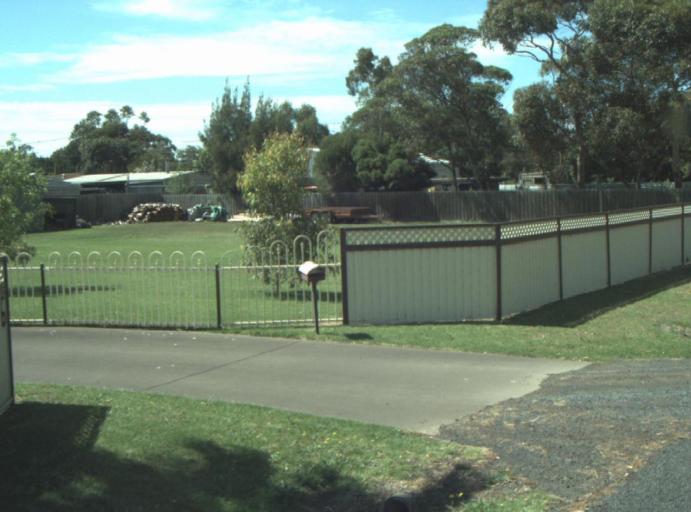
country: AU
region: Victoria
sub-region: Greater Geelong
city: East Geelong
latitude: -38.1710
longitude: 144.4139
